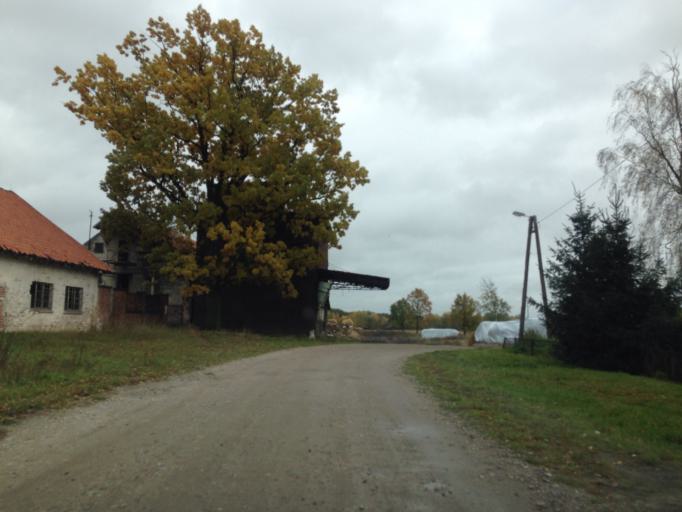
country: PL
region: Pomeranian Voivodeship
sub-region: Powiat kwidzynski
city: Prabuty
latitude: 53.7337
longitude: 19.2103
